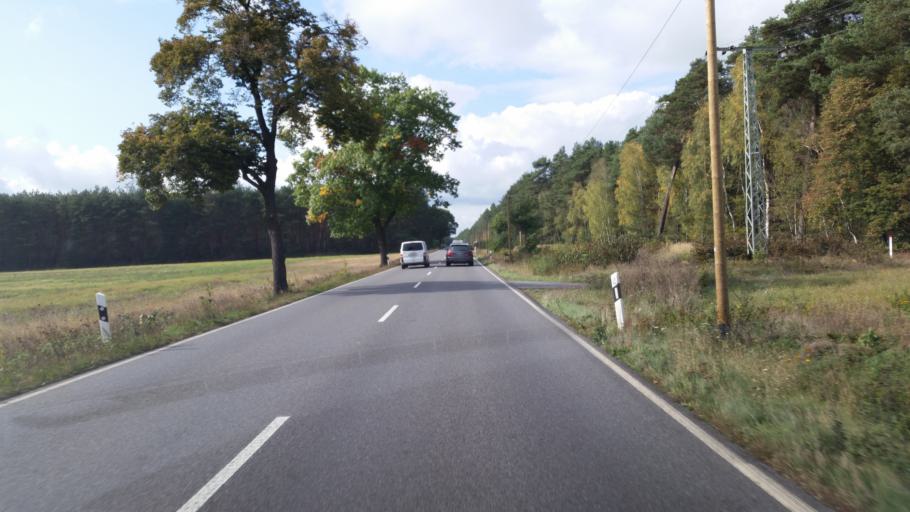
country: DE
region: Brandenburg
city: Grunewald
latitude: 51.4017
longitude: 13.9813
